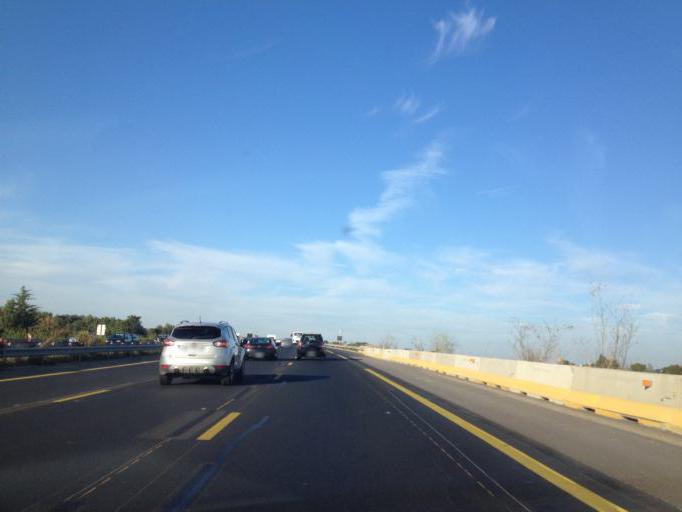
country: FR
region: Languedoc-Roussillon
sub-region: Departement de l'Herault
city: Saint-Aunes
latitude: 43.6314
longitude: 3.9684
